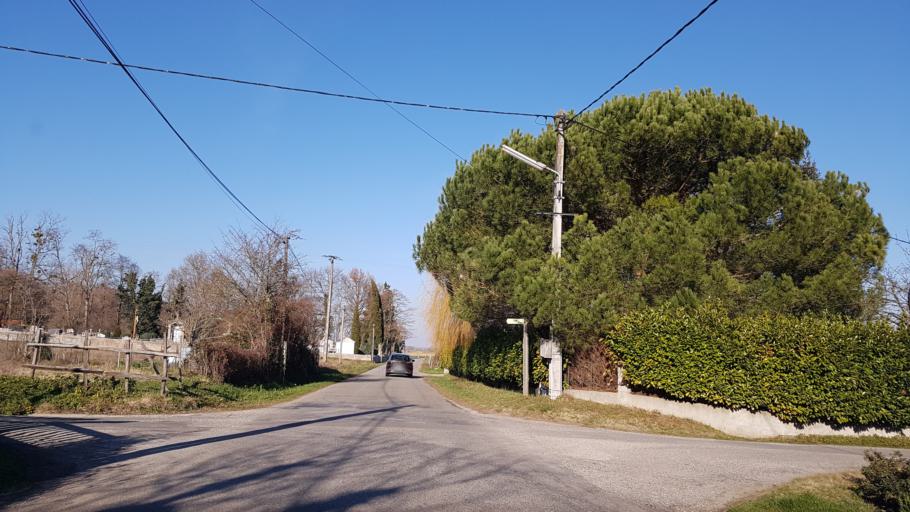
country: FR
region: Midi-Pyrenees
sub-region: Departement de l'Ariege
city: La Tour-du-Crieu
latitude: 43.1128
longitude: 1.7229
